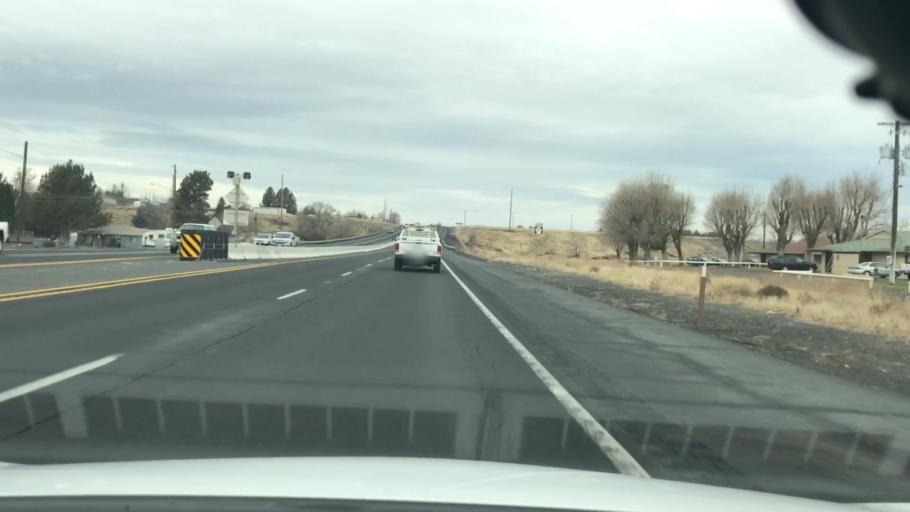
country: US
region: Washington
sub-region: Grant County
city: Moses Lake
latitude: 47.1501
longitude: -119.2953
